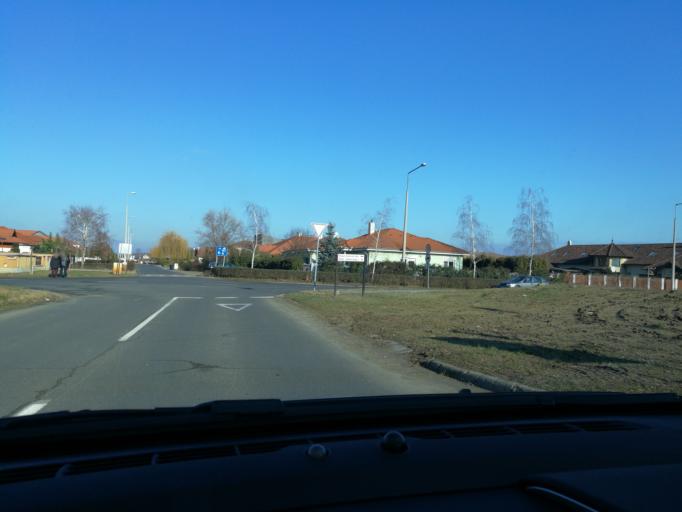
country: HU
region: Szabolcs-Szatmar-Bereg
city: Nyiregyhaza
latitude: 47.9728
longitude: 21.7342
